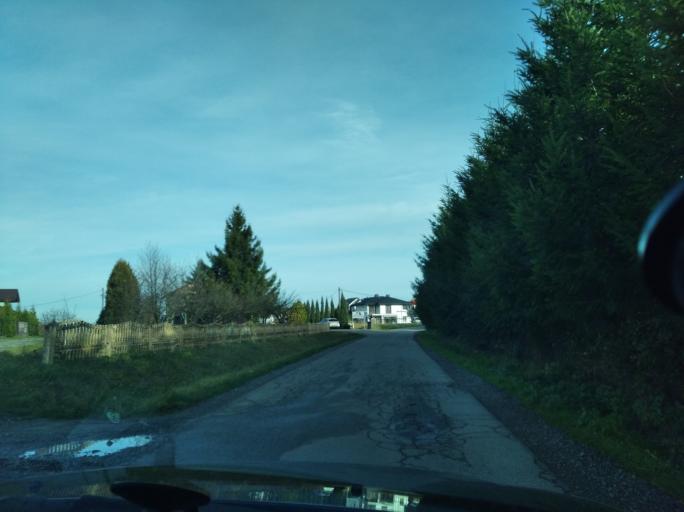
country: PL
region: Subcarpathian Voivodeship
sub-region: Powiat rzeszowski
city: Krasne
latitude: 50.0136
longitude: 22.0971
